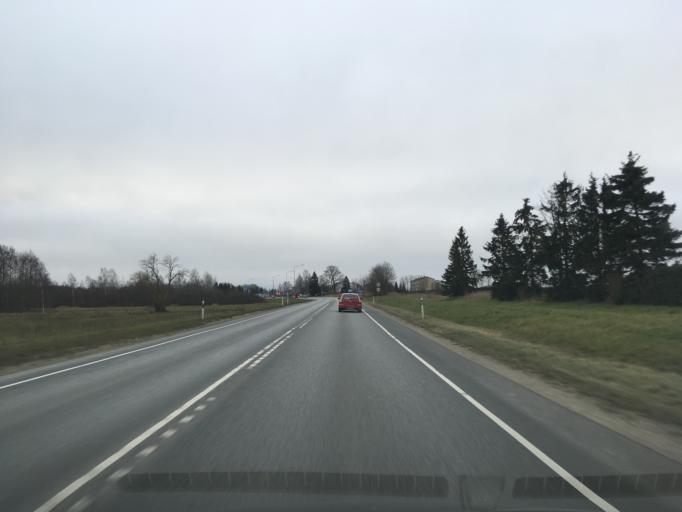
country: EE
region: Laeaene-Virumaa
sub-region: Someru vald
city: Someru
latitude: 59.3688
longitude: 26.4300
